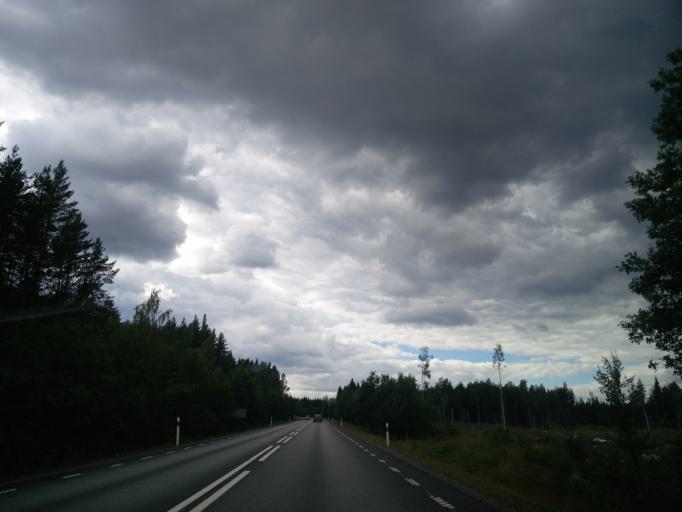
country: SE
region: OErebro
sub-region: Hallefors Kommun
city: Haellefors
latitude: 59.7989
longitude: 14.5686
